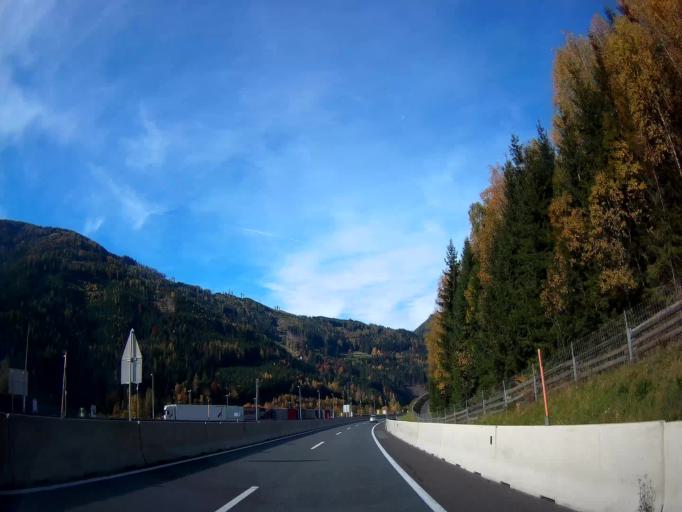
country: AT
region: Styria
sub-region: Politischer Bezirk Leoben
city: Kalwang
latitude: 47.4276
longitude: 14.7245
